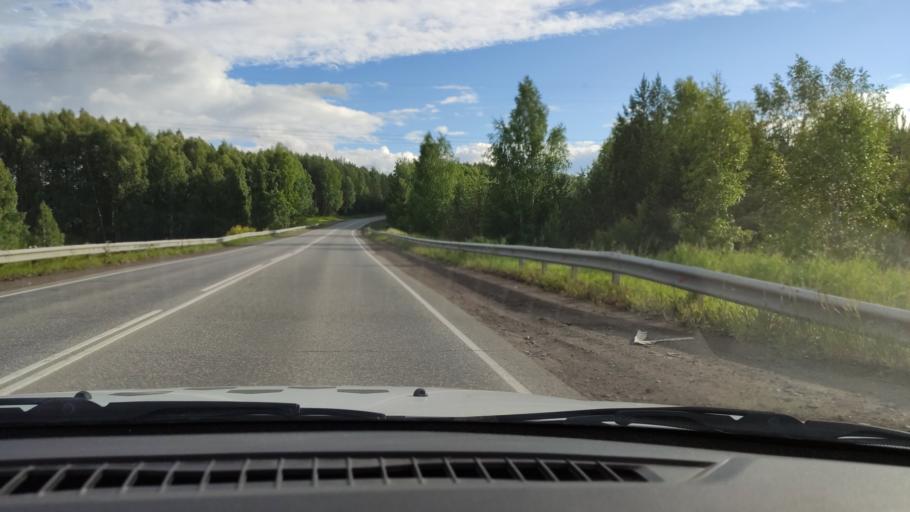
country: RU
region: Perm
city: Kungur
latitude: 57.4151
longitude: 56.9142
